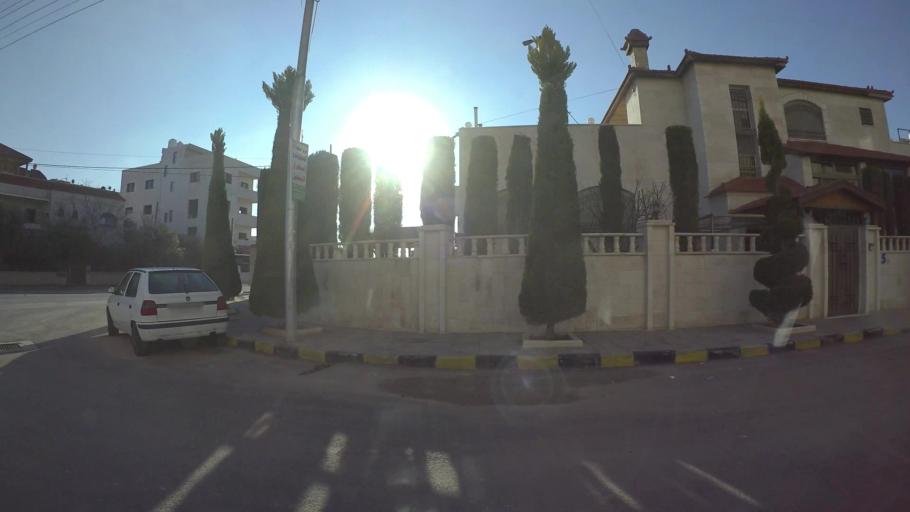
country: JO
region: Amman
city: Al Bunayyat ash Shamaliyah
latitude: 31.8974
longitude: 35.9123
